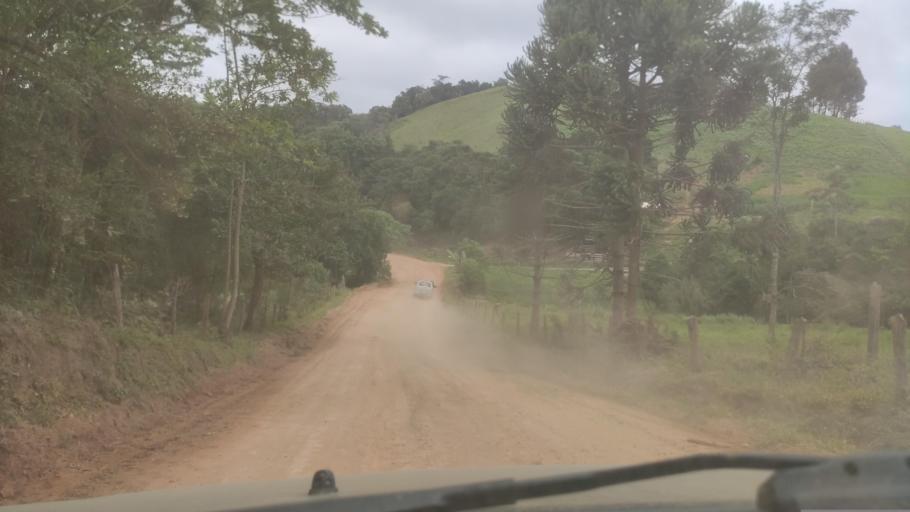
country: BR
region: Minas Gerais
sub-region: Cambui
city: Cambui
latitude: -22.6579
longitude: -45.9058
